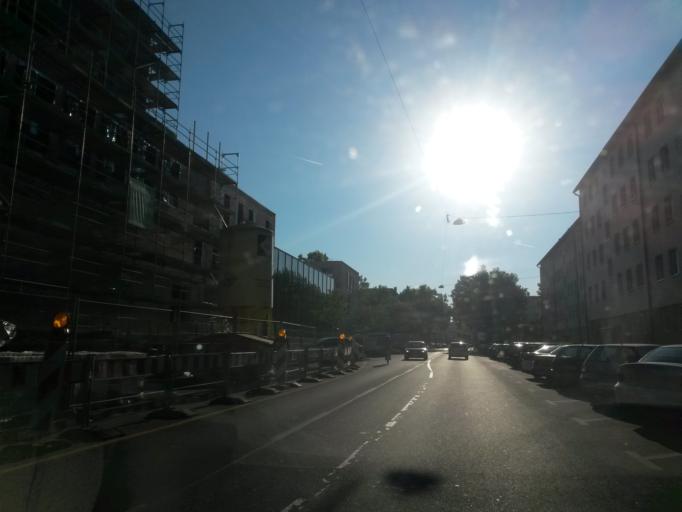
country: DE
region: Bavaria
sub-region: Regierungsbezirk Mittelfranken
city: Furth
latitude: 49.4649
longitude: 10.9933
